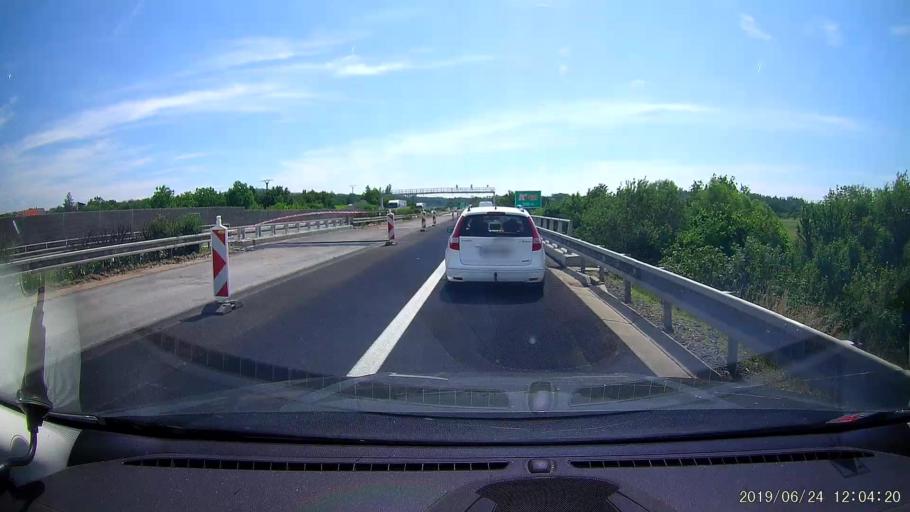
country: CZ
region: Olomoucky
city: Velky Ujezd
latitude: 49.5719
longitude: 17.4803
